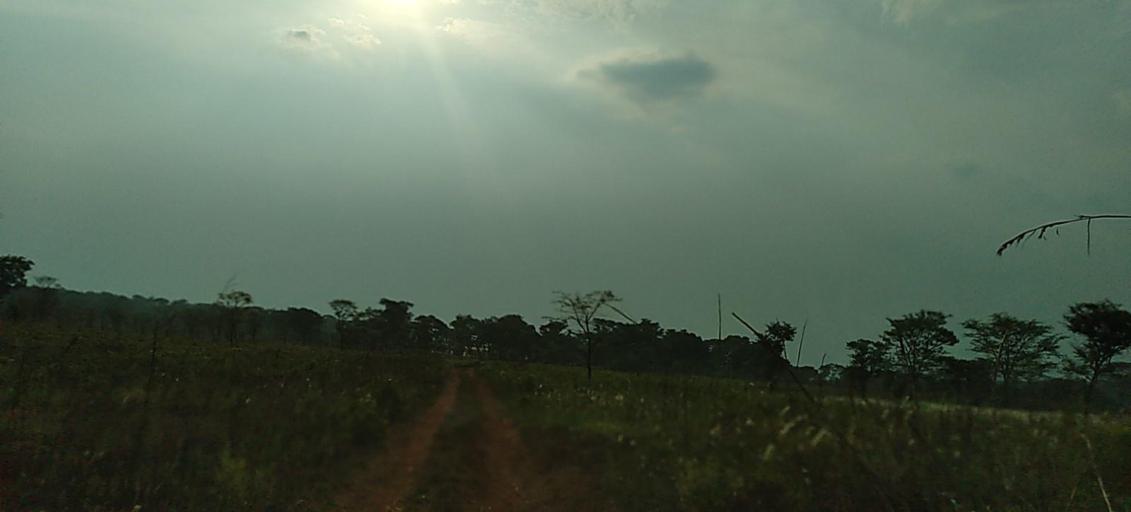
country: ZM
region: North-Western
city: Solwezi
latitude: -12.0467
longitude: 26.0629
